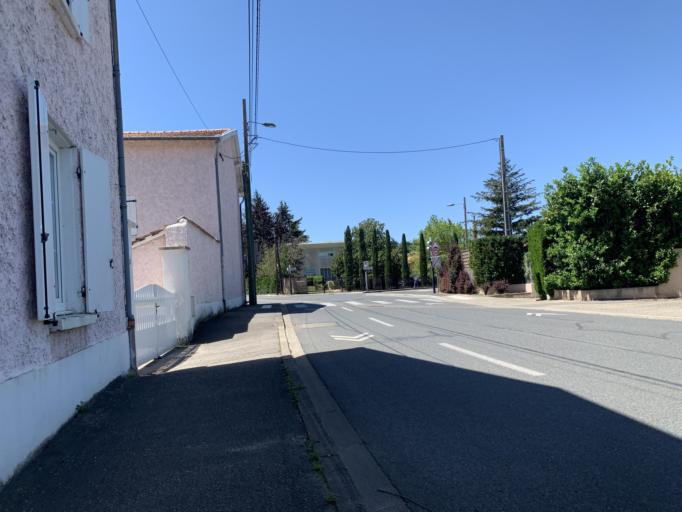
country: FR
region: Rhone-Alpes
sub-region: Departement du Rhone
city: Francheville
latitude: 45.7364
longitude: 4.7529
